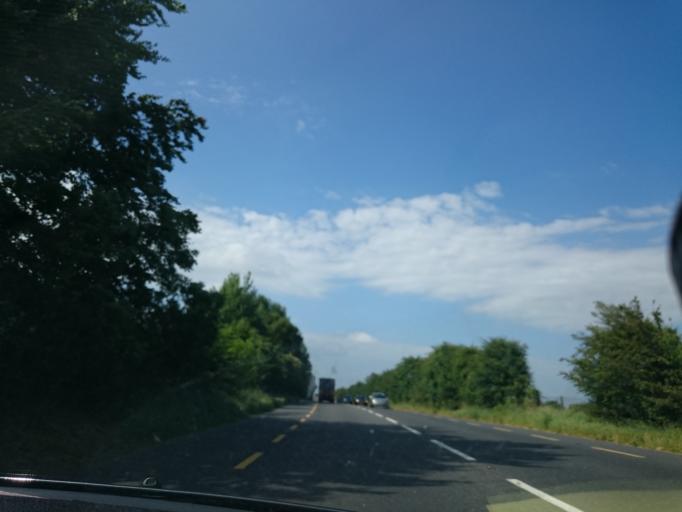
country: IE
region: Leinster
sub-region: Kilkenny
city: Kilkenny
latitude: 52.5983
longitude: -7.2417
